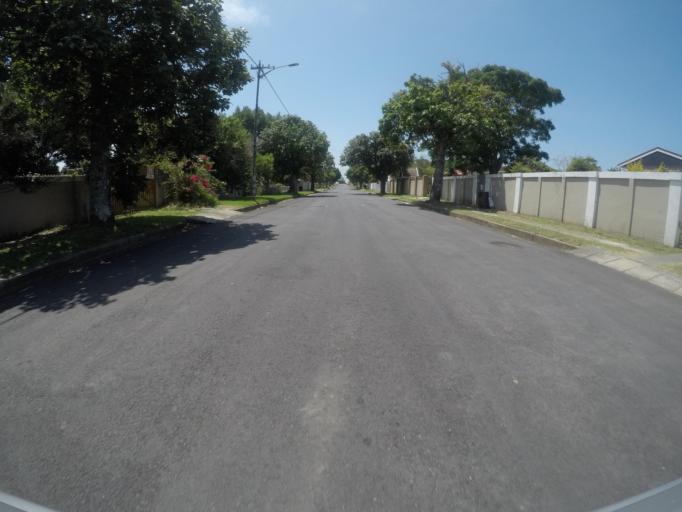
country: ZA
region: Eastern Cape
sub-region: Buffalo City Metropolitan Municipality
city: East London
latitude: -32.9747
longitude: 27.8788
